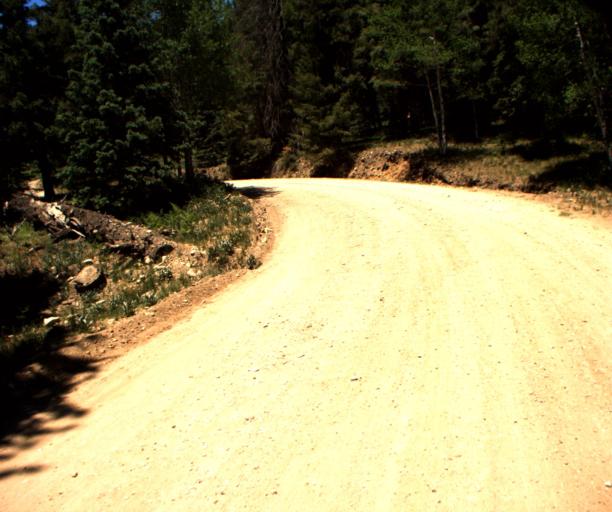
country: US
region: Arizona
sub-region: Graham County
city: Swift Trail Junction
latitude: 32.6671
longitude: -109.8727
